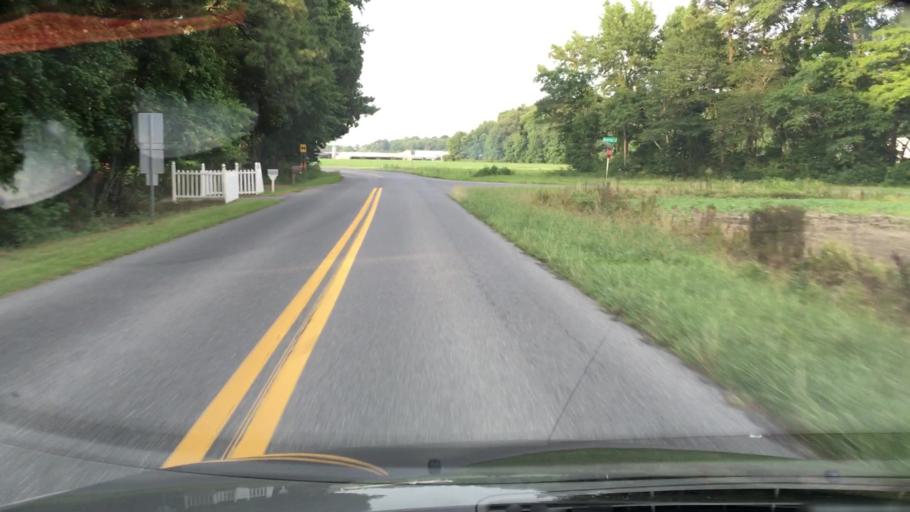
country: US
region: Maryland
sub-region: Worcester County
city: Ocean Pines
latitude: 38.4700
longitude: -75.1416
